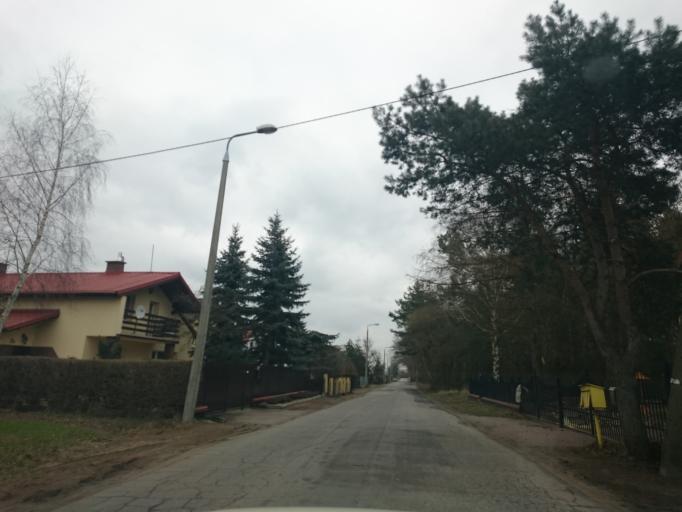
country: PL
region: Kujawsko-Pomorskie
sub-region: Powiat torunski
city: Lubicz Gorny
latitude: 53.0390
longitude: 18.8027
